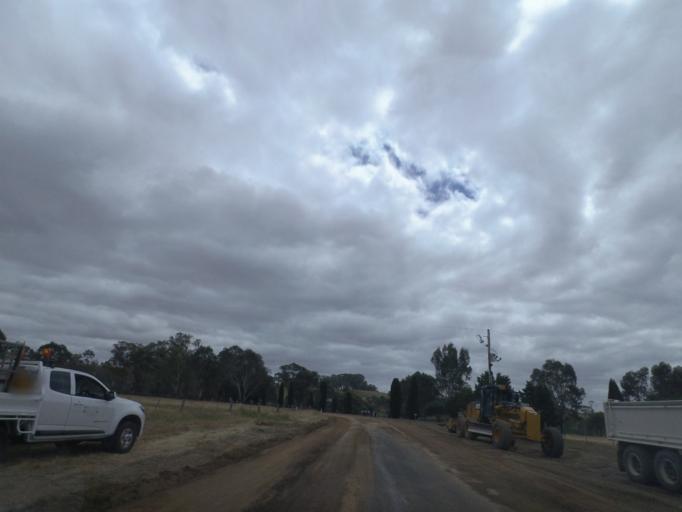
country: AU
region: Victoria
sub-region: Whittlesea
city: Whittlesea
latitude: -37.1134
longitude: 145.0244
